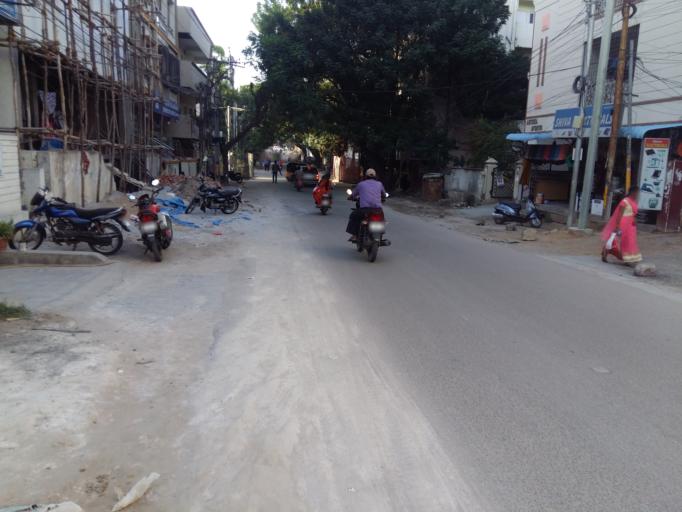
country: IN
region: Telangana
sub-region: Rangareddi
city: Kukatpalli
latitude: 17.4895
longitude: 78.3961
